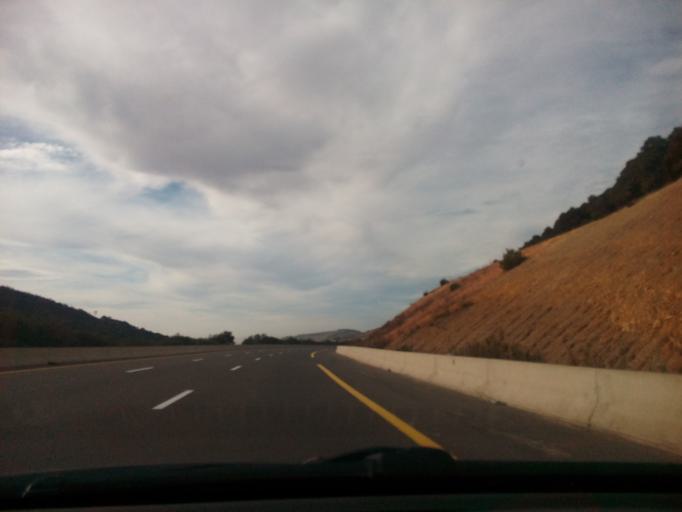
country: DZ
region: Sidi Bel Abbes
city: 'Ain el Berd
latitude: 35.3890
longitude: -0.4896
